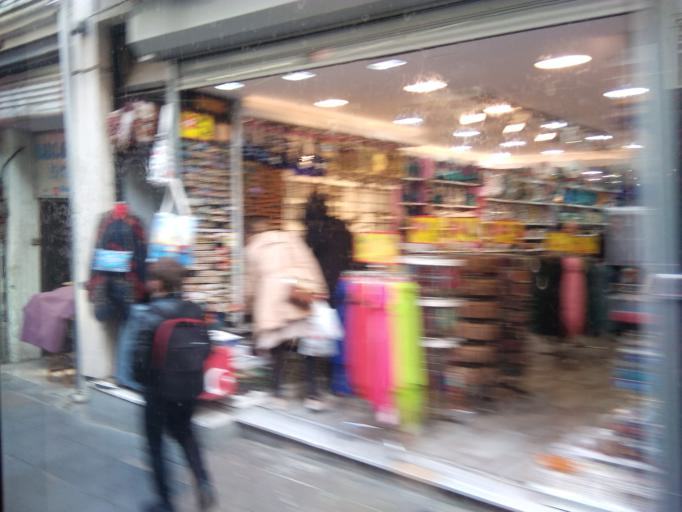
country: TR
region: Istanbul
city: Eminoenue
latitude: 41.0127
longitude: 28.9784
